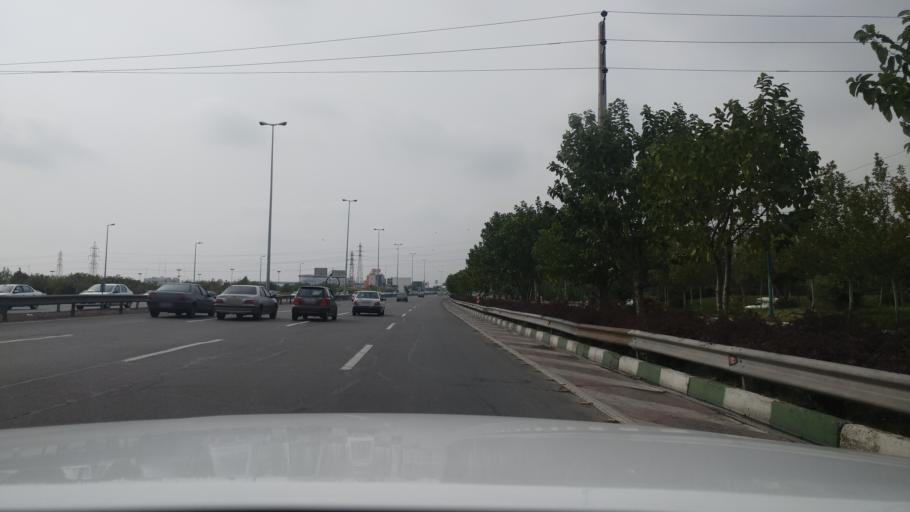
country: IR
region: Tehran
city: Shahr-e Qods
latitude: 35.7147
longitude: 51.2503
